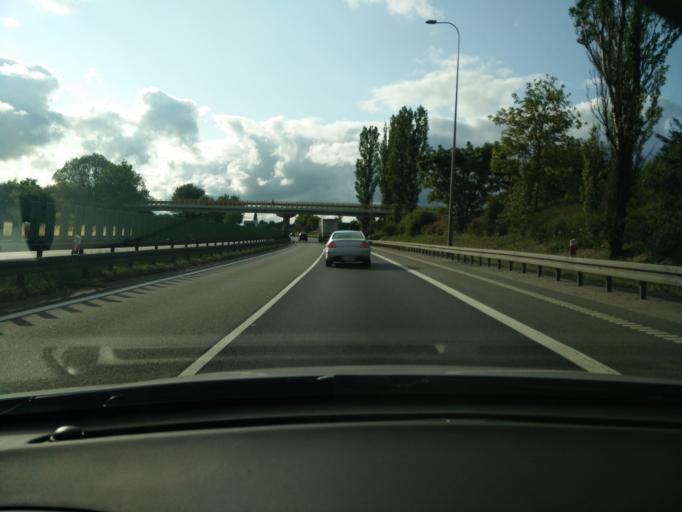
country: PL
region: Pomeranian Voivodeship
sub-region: Powiat gdanski
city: Kowale
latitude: 54.2970
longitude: 18.5820
